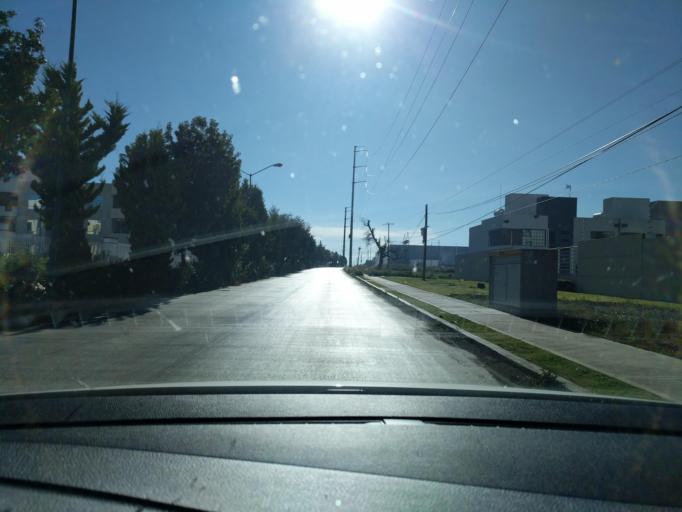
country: MX
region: Puebla
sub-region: Huejotzingo
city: Los Encinos
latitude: 19.1736
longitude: -98.3828
